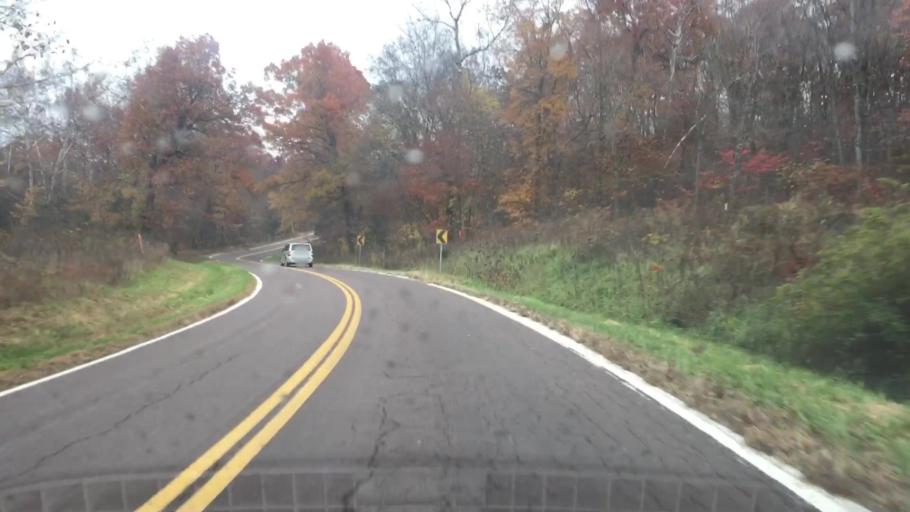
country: US
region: Missouri
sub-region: Callaway County
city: Fulton
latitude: 38.7892
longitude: -91.7510
